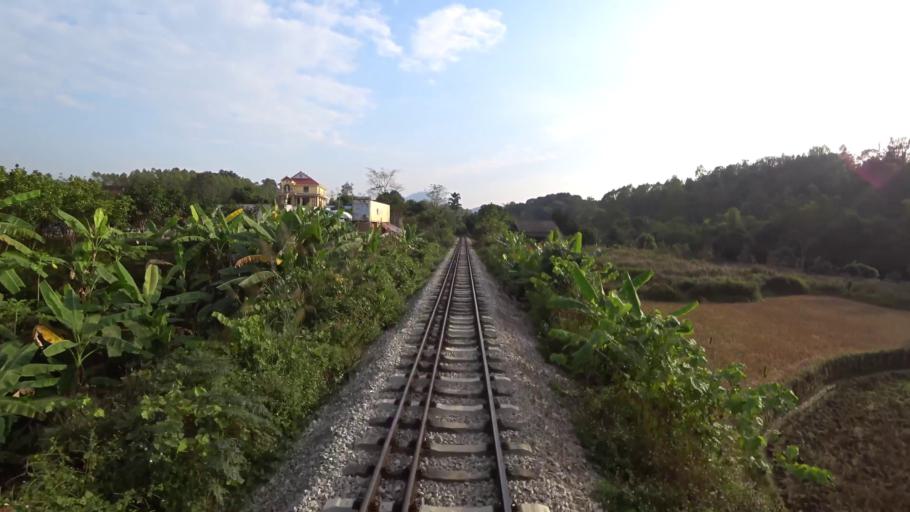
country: VN
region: Lang Son
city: Thi Tran Cao Loc
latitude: 21.9321
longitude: 106.6998
